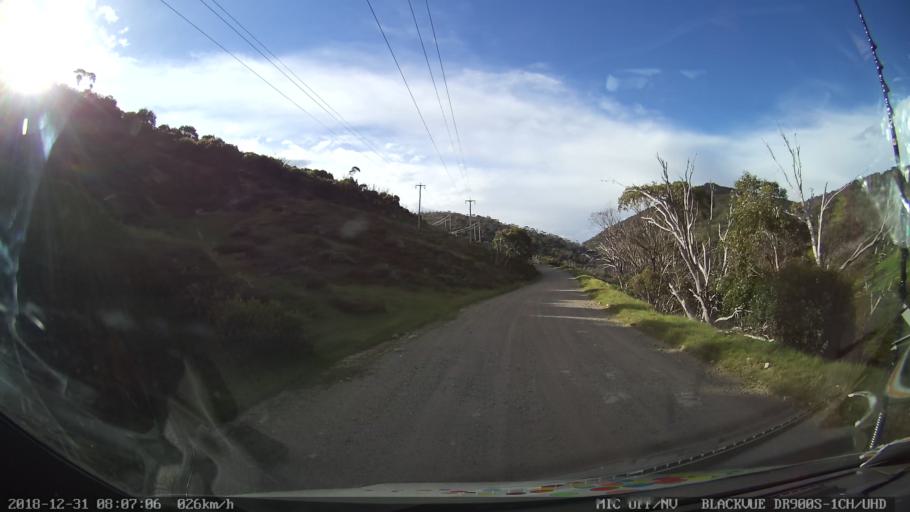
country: AU
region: New South Wales
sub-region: Snowy River
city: Jindabyne
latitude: -36.3773
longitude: 148.4089
